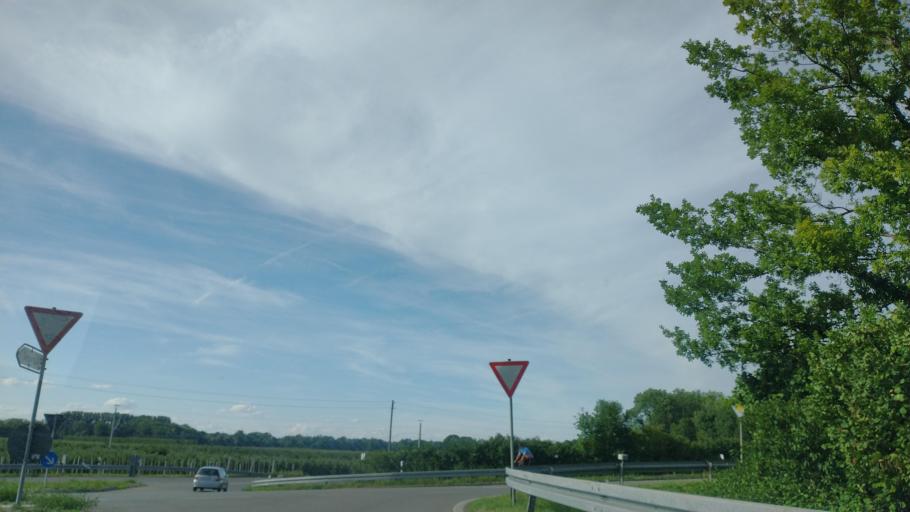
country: DE
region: Baden-Wuerttemberg
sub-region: Tuebingen Region
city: Kressbronn am Bodensee
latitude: 47.5960
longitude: 9.5761
